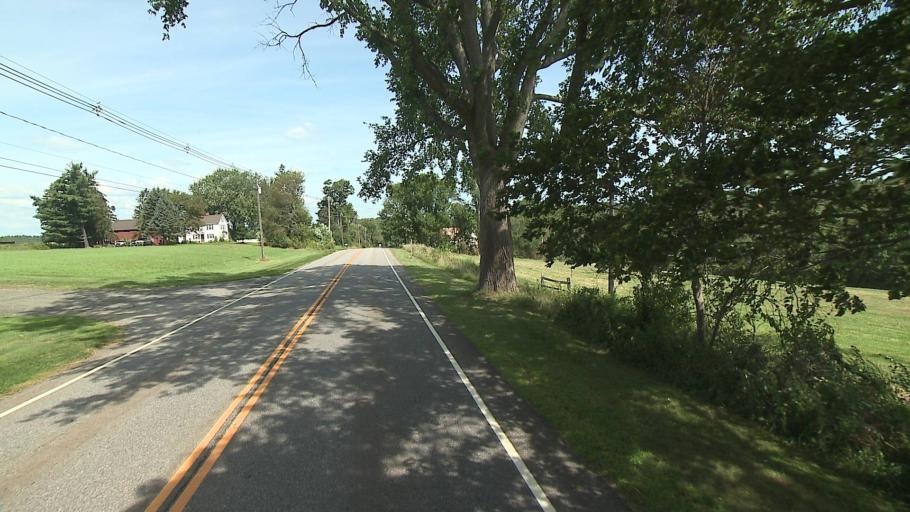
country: US
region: Connecticut
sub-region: Litchfield County
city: Bethlehem Village
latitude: 41.6670
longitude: -73.1986
